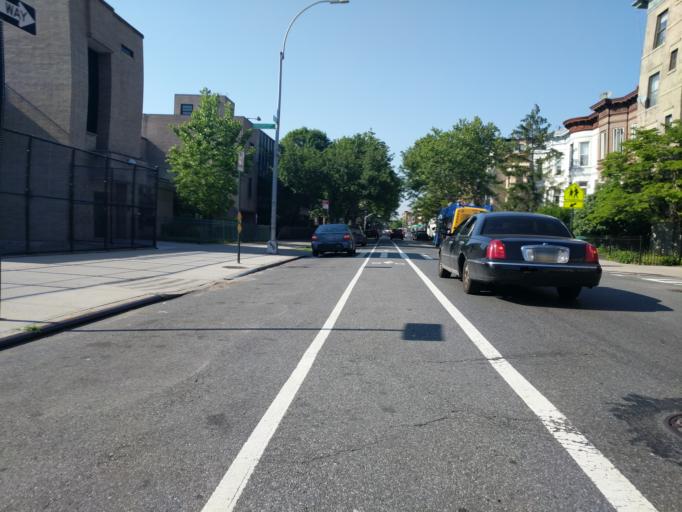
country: US
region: New York
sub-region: Kings County
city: Brooklyn
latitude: 40.6737
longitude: -73.9419
